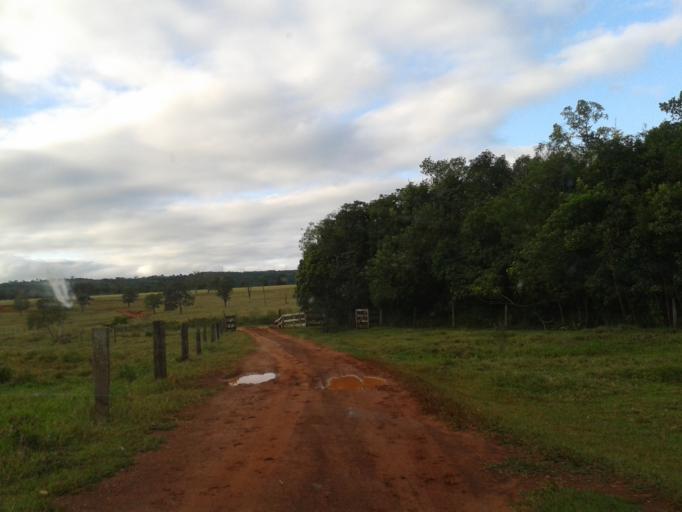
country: BR
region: Minas Gerais
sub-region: Campina Verde
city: Campina Verde
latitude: -19.4733
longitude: -49.6511
